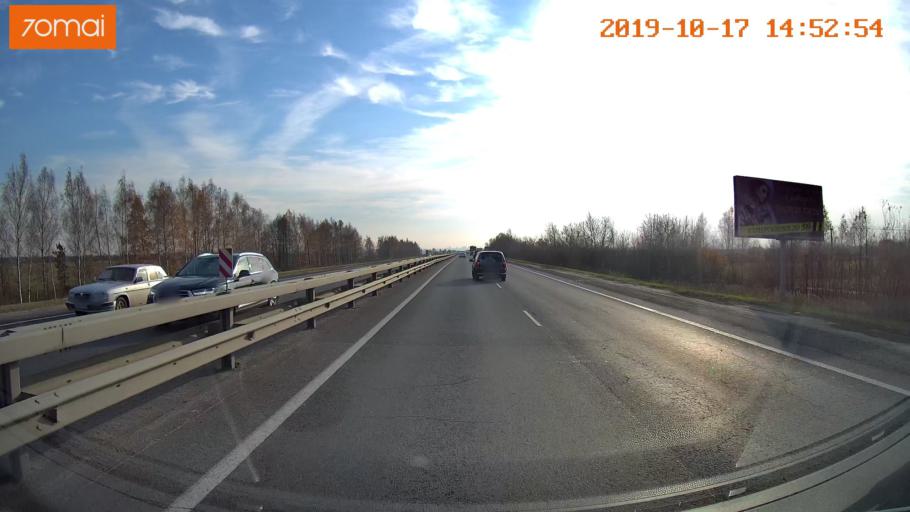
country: RU
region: Rjazan
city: Polyany
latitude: 54.7012
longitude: 39.8425
